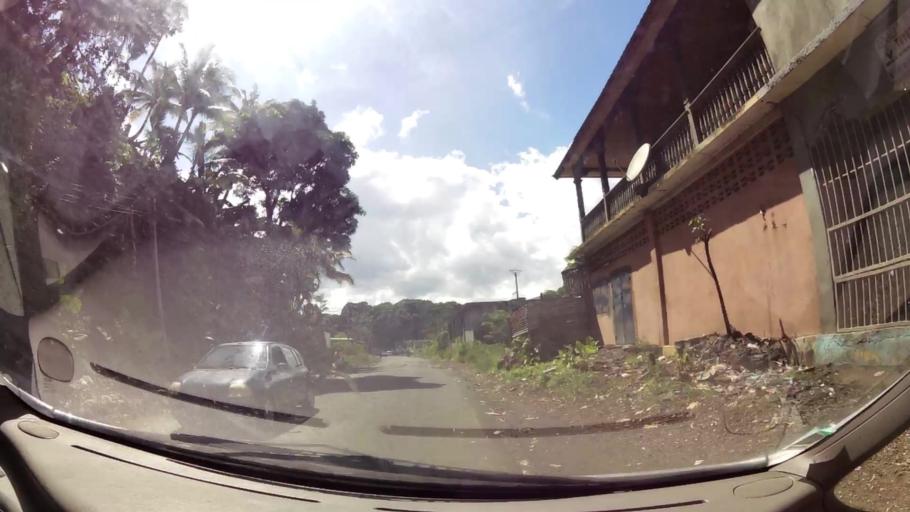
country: KM
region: Grande Comore
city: Mavingouni
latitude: -11.7236
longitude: 43.2502
